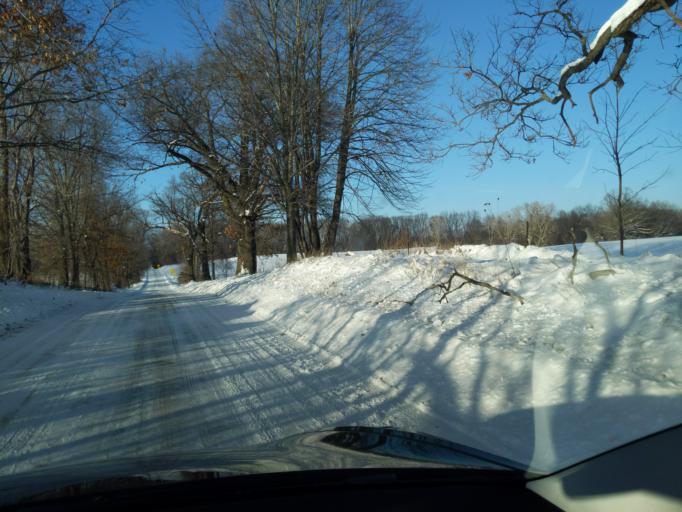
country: US
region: Michigan
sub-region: Ingham County
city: Stockbridge
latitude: 42.4577
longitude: -84.1185
